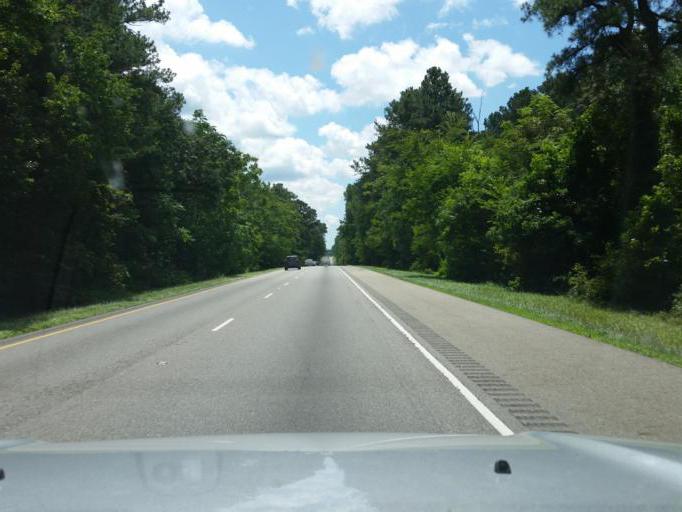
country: US
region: Virginia
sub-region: City of Williamsburg
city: Williamsburg
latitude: 37.3145
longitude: -76.6918
